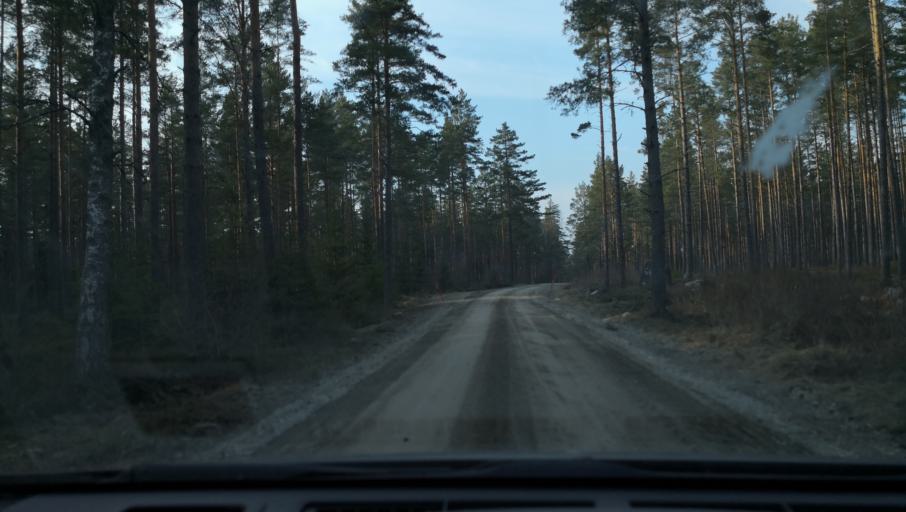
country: SE
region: OErebro
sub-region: Lindesbergs Kommun
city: Frovi
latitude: 59.3636
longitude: 15.3280
